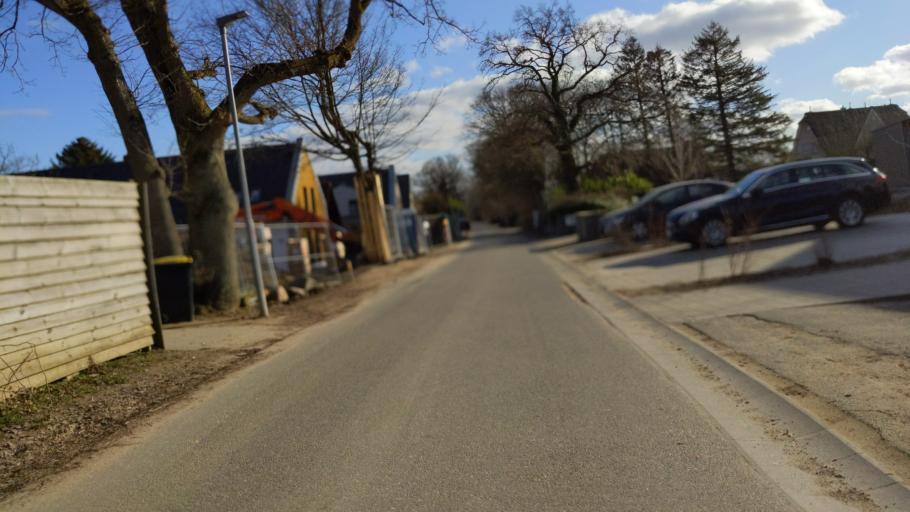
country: DE
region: Schleswig-Holstein
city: Timmendorfer Strand
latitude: 54.0010
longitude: 10.7551
